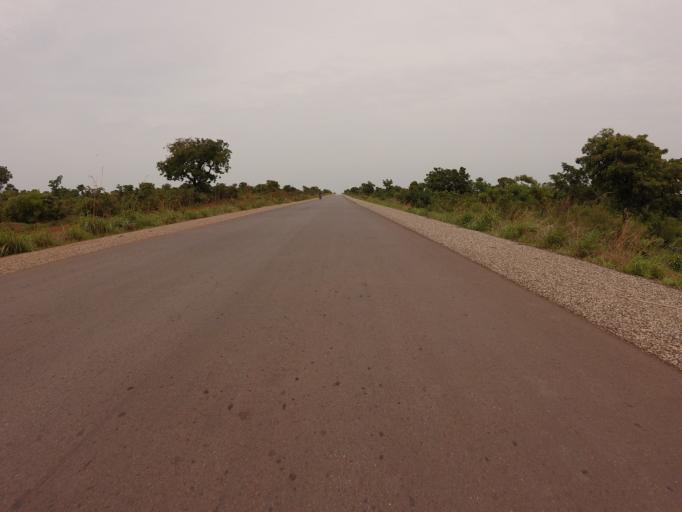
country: GH
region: Northern
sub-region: Yendi
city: Yendi
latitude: 8.9591
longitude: -0.0173
